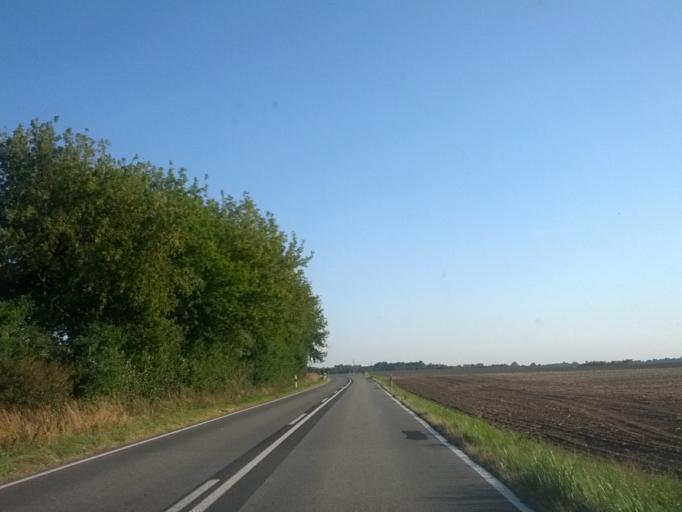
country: DE
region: Mecklenburg-Vorpommern
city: Brandshagen
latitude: 54.1768
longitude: 13.1817
